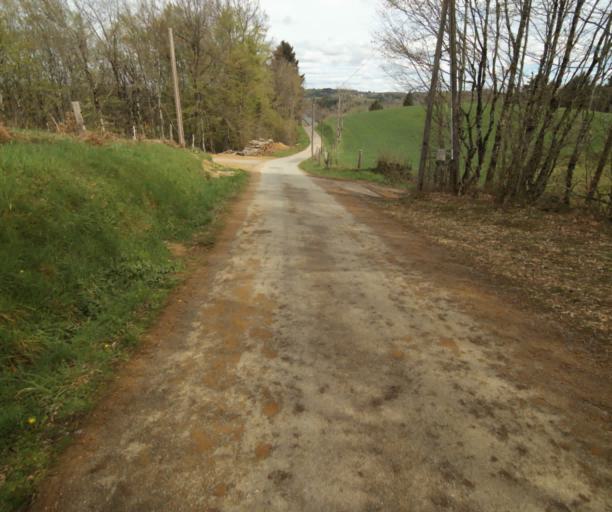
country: FR
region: Limousin
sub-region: Departement de la Correze
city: Laguenne
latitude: 45.2289
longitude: 1.8496
